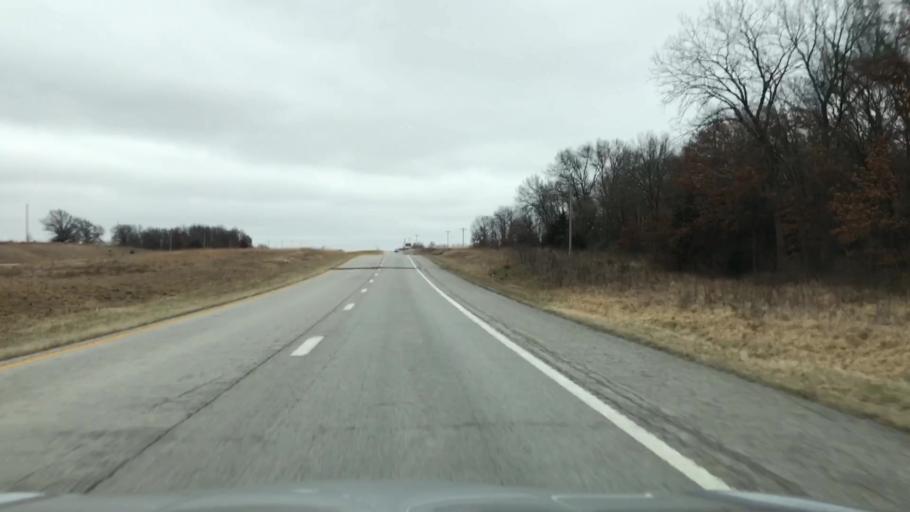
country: US
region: Missouri
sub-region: Linn County
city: Linneus
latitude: 39.7781
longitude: -93.1890
